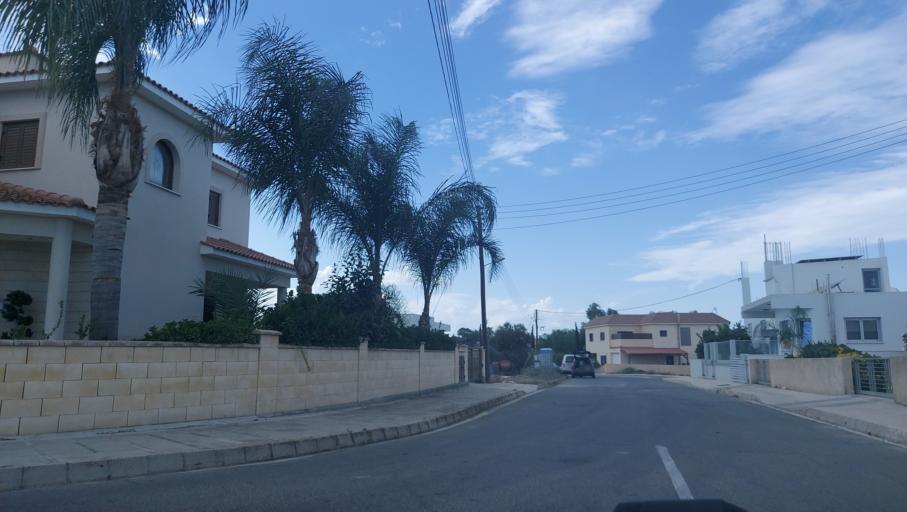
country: CY
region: Lefkosia
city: Pano Deftera
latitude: 35.0859
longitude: 33.2673
